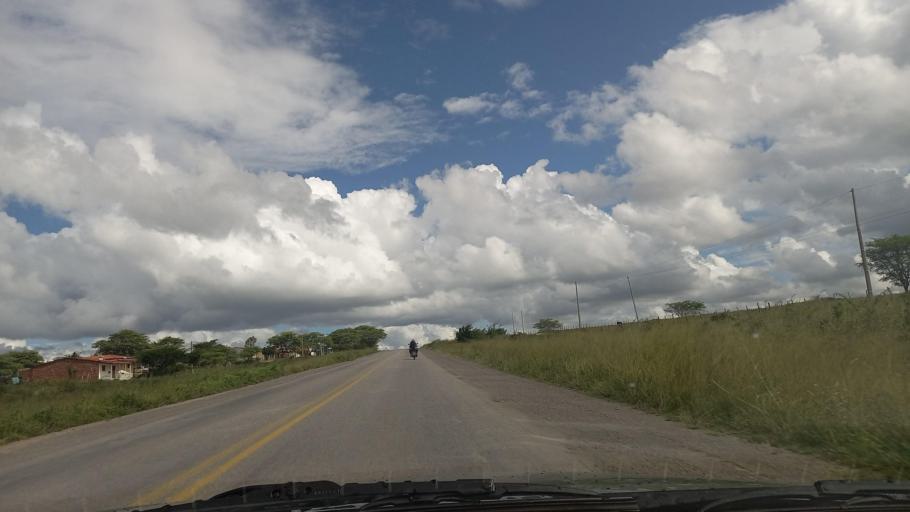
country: BR
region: Pernambuco
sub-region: Lajedo
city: Lajedo
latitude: -8.6046
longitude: -36.2932
